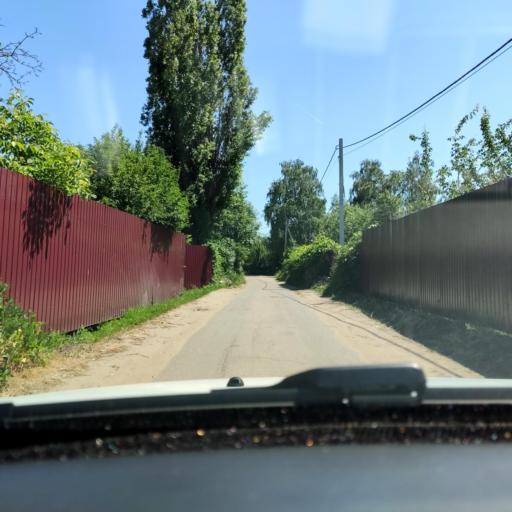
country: RU
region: Voronezj
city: Shilovo
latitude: 51.5918
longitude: 39.1474
